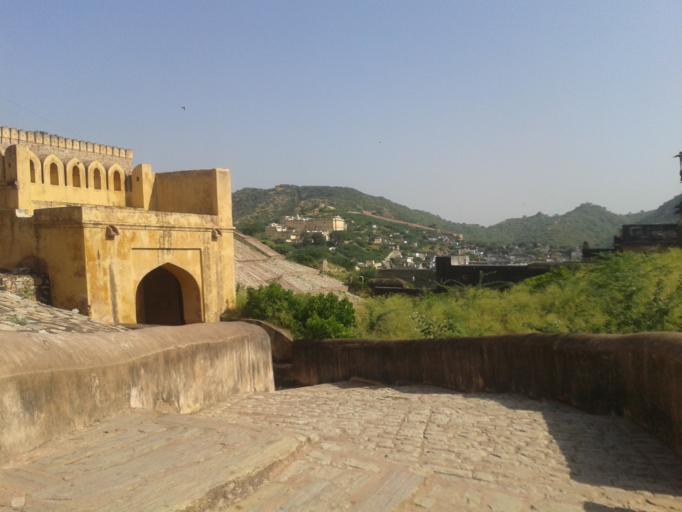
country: IN
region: Rajasthan
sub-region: Jaipur
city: Jaipur
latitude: 26.9866
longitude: 75.8523
